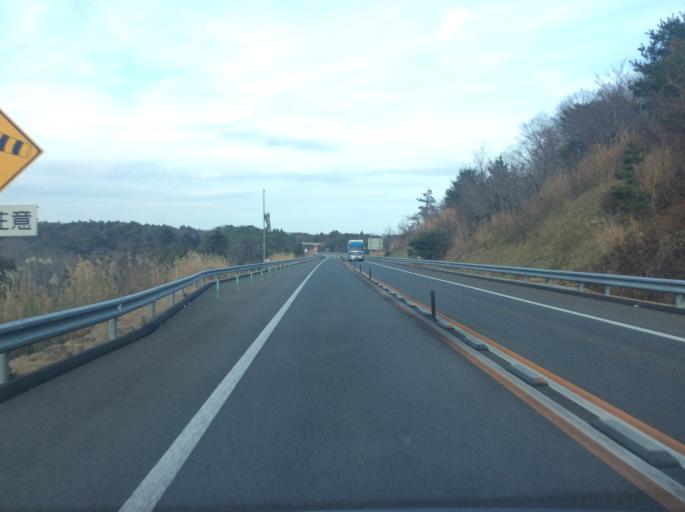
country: JP
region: Fukushima
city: Iwaki
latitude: 37.2471
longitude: 140.9886
